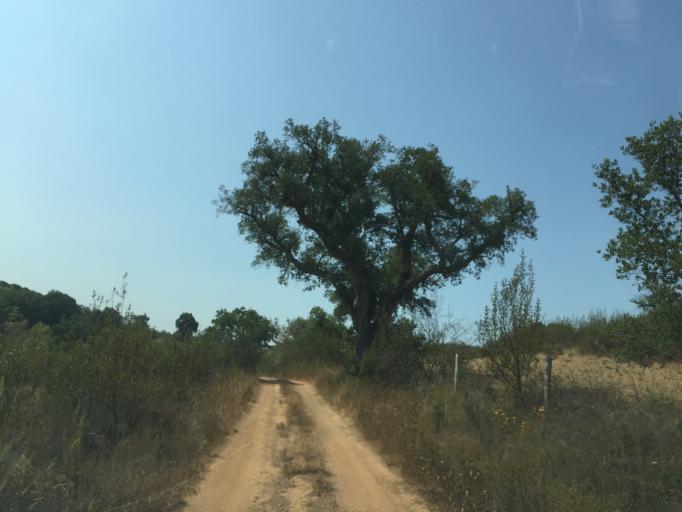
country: PT
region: Setubal
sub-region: Santiago do Cacem
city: Santiago do Cacem
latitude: 37.9735
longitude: -8.5160
